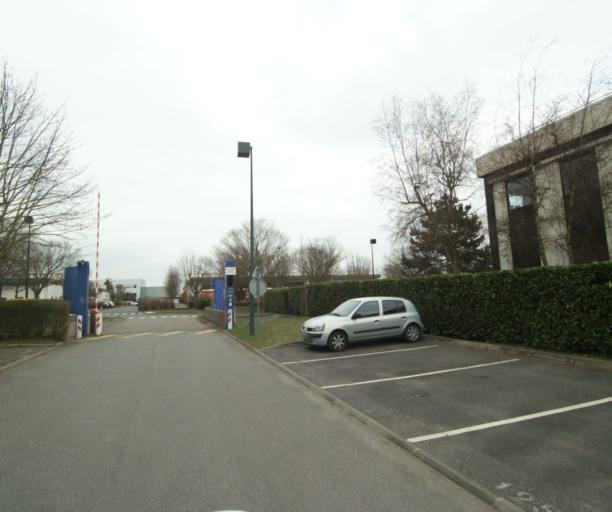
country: FR
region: Ile-de-France
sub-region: Departement du Val-d'Oise
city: Vaureal
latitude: 49.0551
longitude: 2.0353
